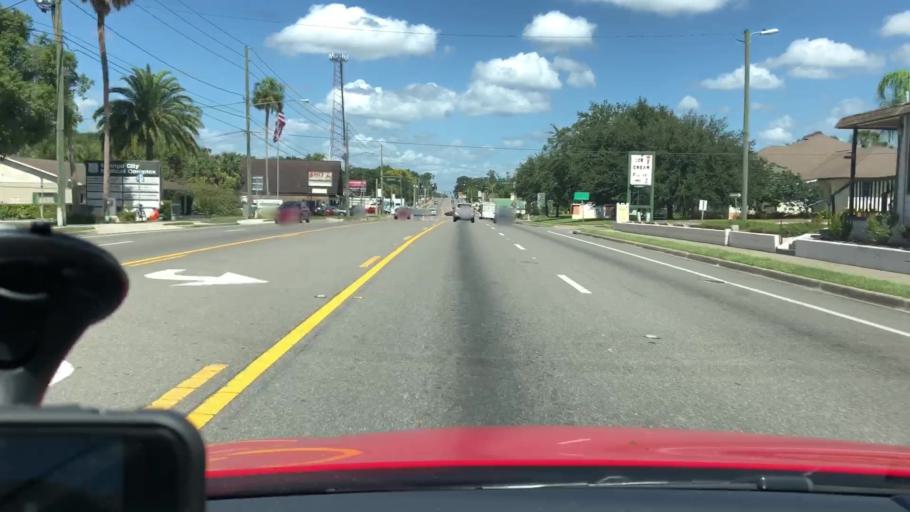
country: US
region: Florida
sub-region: Volusia County
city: Orange City
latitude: 28.9471
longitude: -81.2988
